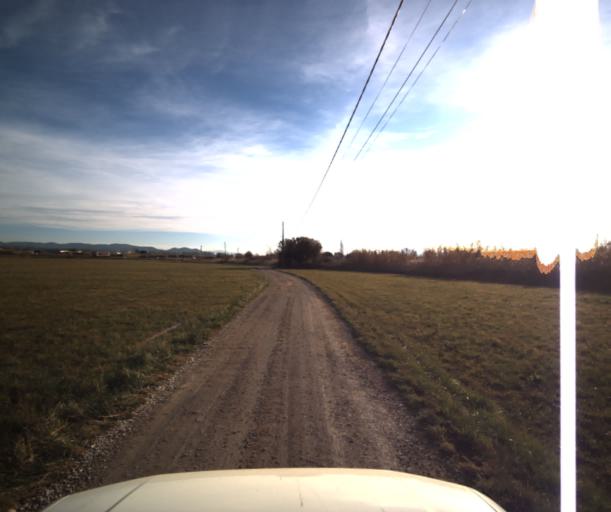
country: FR
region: Provence-Alpes-Cote d'Azur
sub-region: Departement du Vaucluse
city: Pertuis
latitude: 43.6779
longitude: 5.4860
